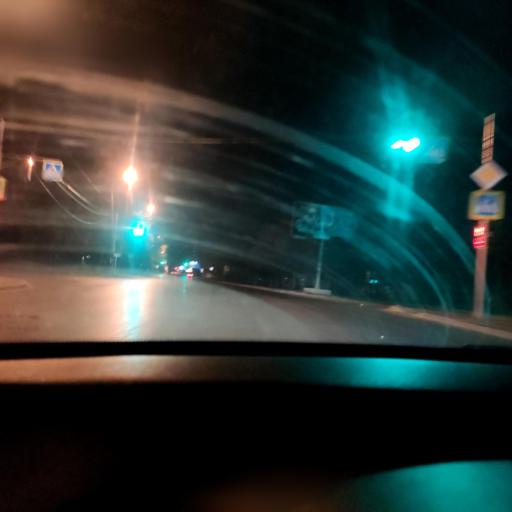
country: RU
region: Samara
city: Samara
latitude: 53.2142
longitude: 50.2121
